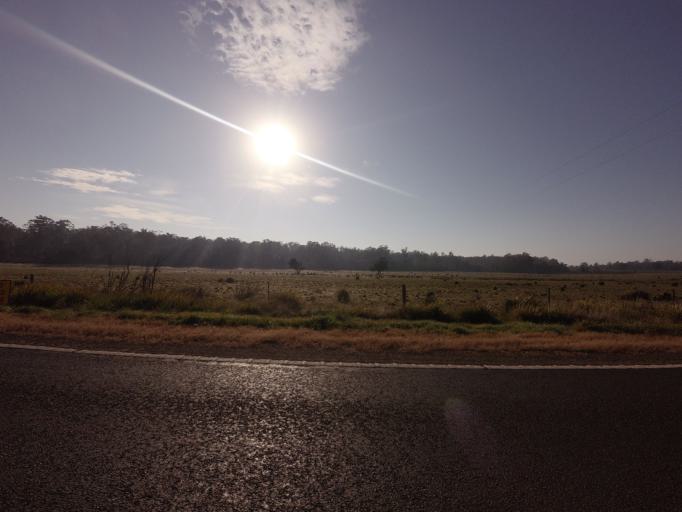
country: AU
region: Tasmania
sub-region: Northern Midlands
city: Longford
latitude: -41.5320
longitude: 147.0406
